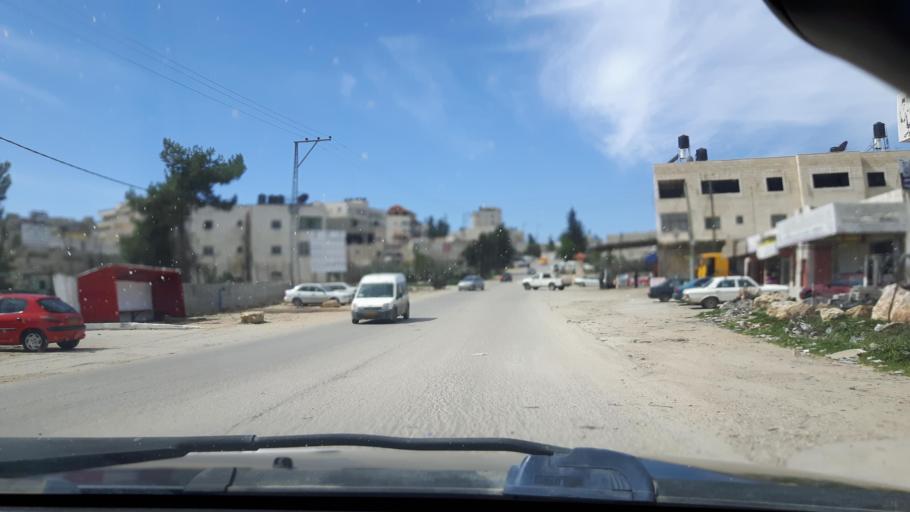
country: PS
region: West Bank
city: Al Judayrah
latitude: 31.8528
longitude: 35.1917
